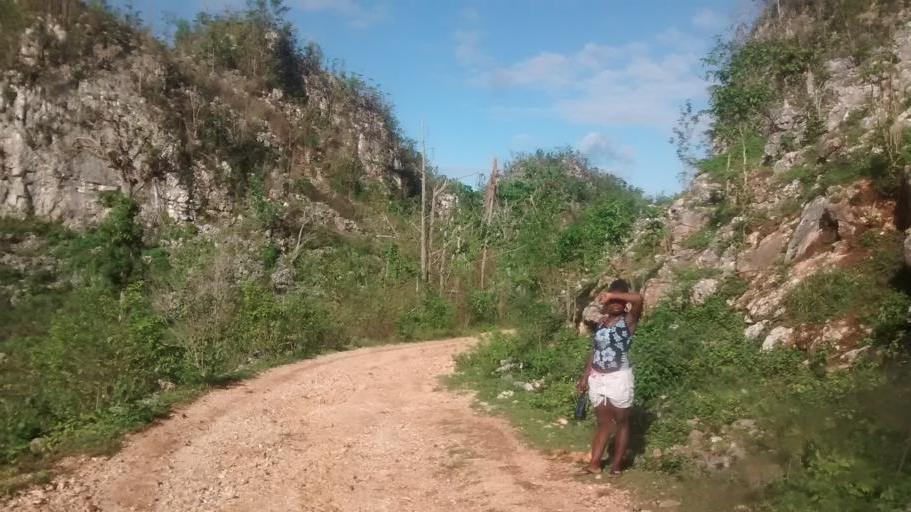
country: HT
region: Grandans
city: Corail
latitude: 18.5309
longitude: -73.8451
